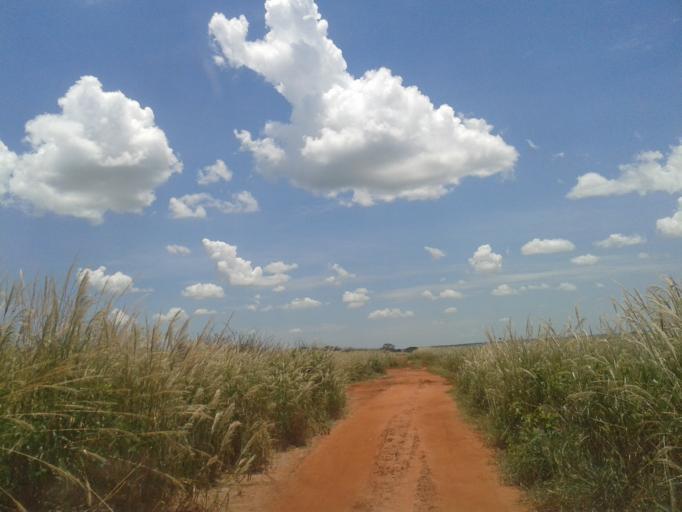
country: BR
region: Minas Gerais
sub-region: Santa Vitoria
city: Santa Vitoria
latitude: -19.2259
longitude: -50.4883
